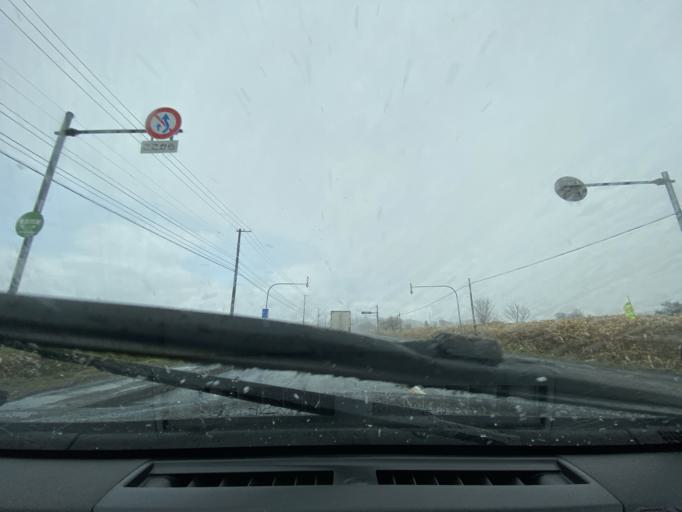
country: JP
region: Hokkaido
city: Takikawa
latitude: 43.6377
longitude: 141.9471
